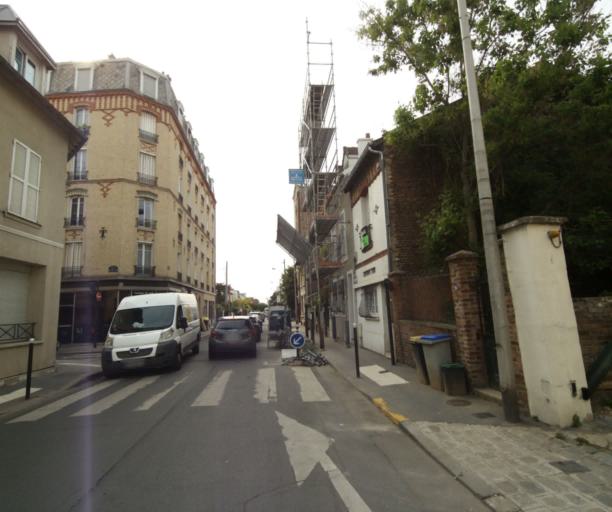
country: FR
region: Ile-de-France
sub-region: Departement des Hauts-de-Seine
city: Bois-Colombes
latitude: 48.9209
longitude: 2.2698
